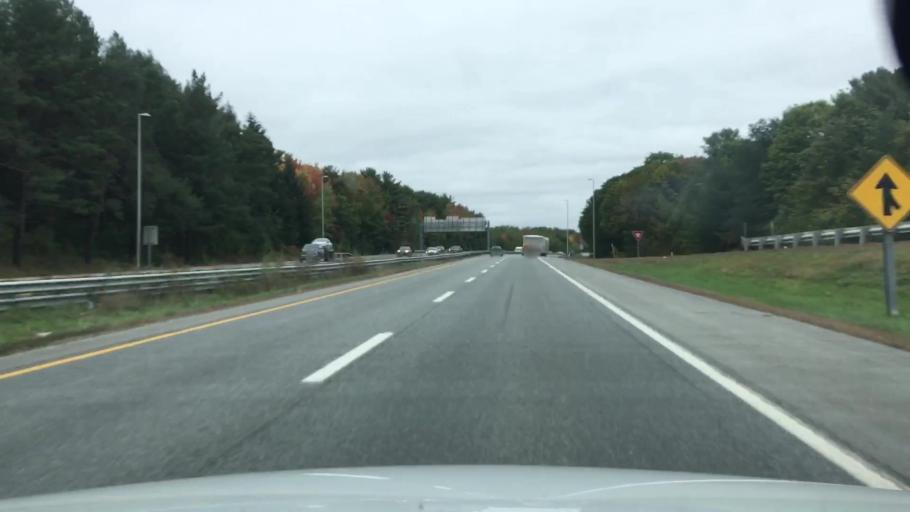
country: US
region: Maine
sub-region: Penobscot County
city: Bangor
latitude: 44.8003
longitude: -68.8012
